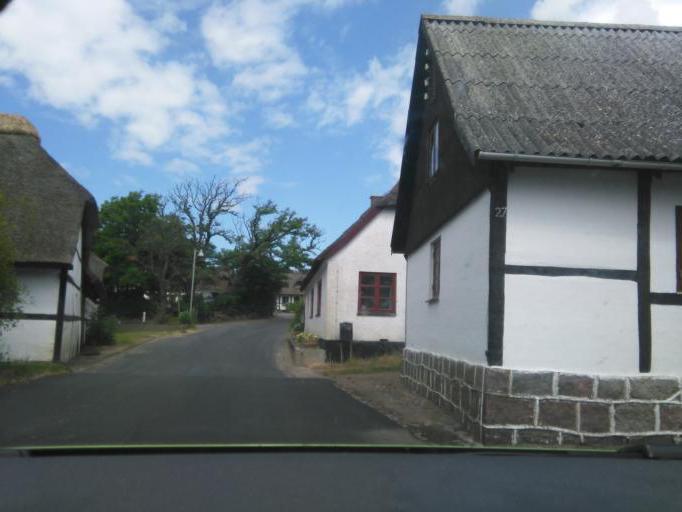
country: DK
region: Zealand
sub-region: Kalundborg Kommune
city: Gorlev
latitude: 55.5247
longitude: 11.1106
